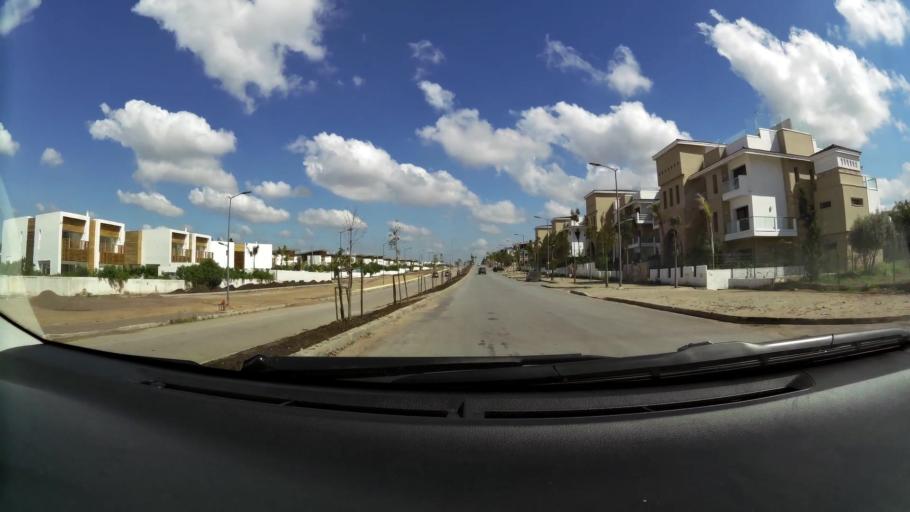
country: MA
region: Grand Casablanca
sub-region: Nouaceur
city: Bouskoura
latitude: 33.4849
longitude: -7.5966
